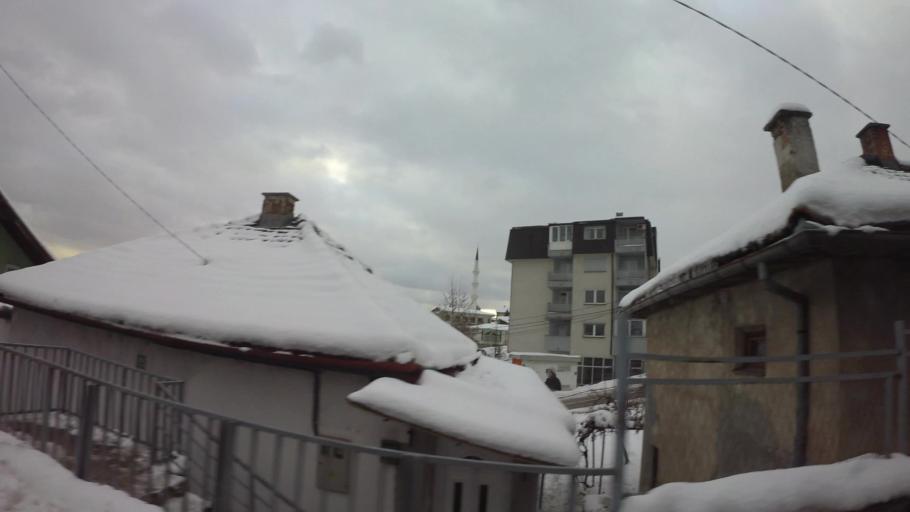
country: BA
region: Federation of Bosnia and Herzegovina
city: Kobilja Glava
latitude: 43.8618
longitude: 18.3851
